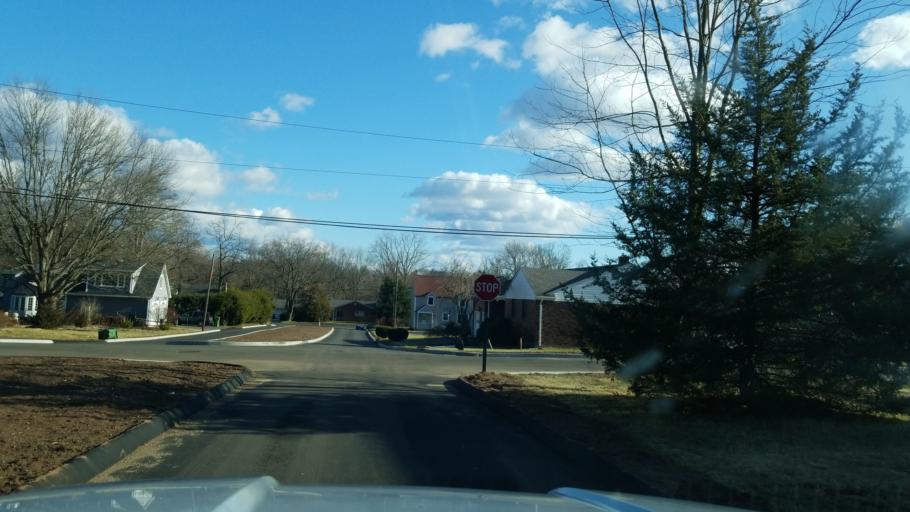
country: US
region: Connecticut
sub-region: Middlesex County
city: Middletown
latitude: 41.5593
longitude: -72.6763
